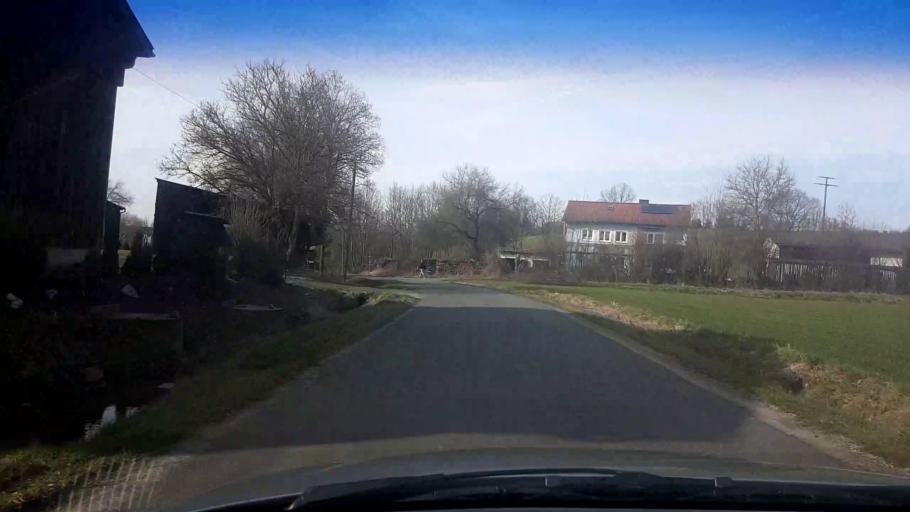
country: DE
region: Bavaria
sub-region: Upper Franconia
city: Burgebrach
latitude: 49.8177
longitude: 10.7494
